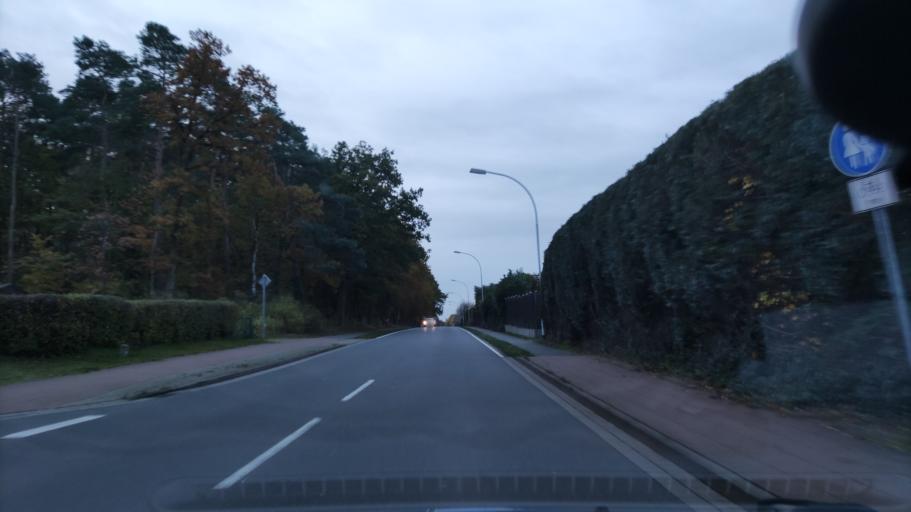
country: DE
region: Lower Saxony
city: Munster
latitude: 53.0067
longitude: 10.0881
